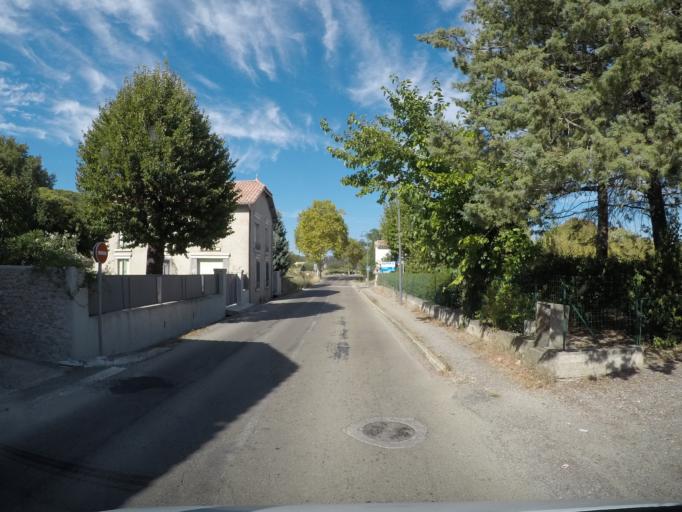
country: FR
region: Languedoc-Roussillon
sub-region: Departement du Gard
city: Boisset-et-Gaujac
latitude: 44.0236
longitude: 3.9972
